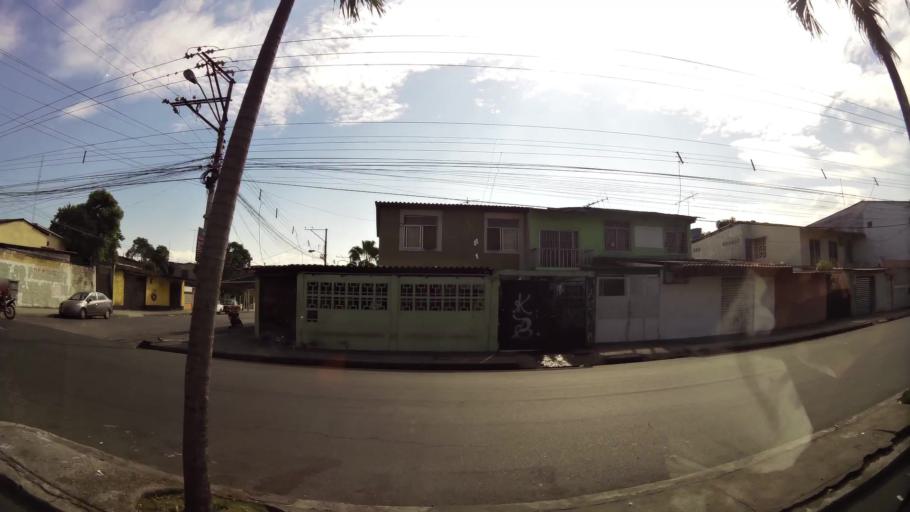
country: EC
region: Guayas
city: Guayaquil
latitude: -2.2066
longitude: -79.9118
